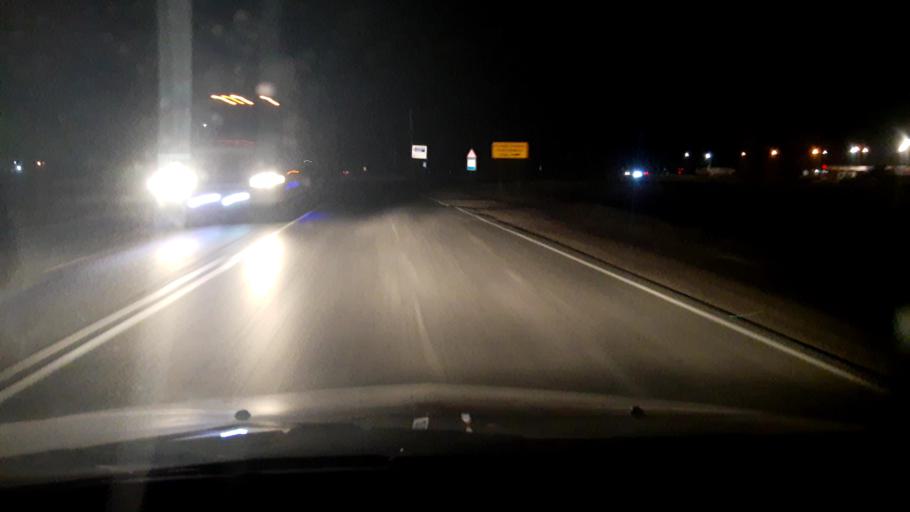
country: RU
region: Bashkortostan
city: Iglino
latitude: 54.7679
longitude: 56.2614
